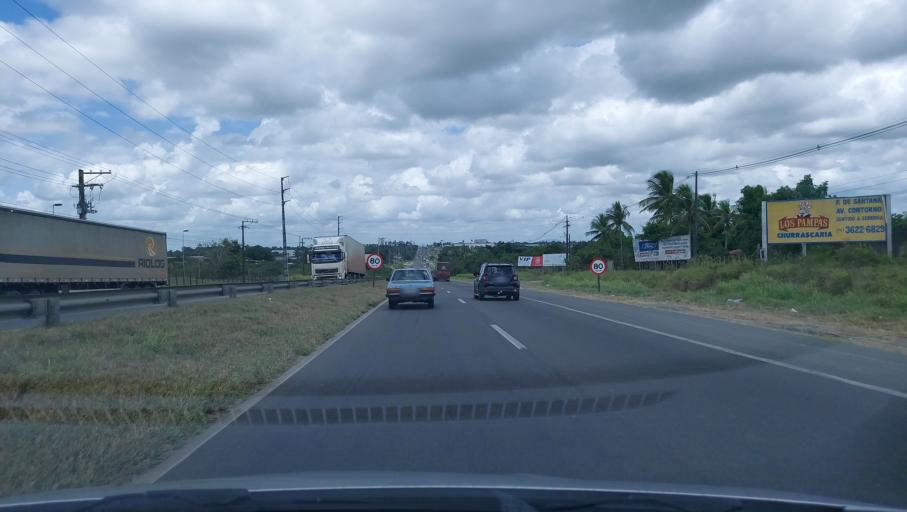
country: BR
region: Bahia
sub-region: Conceicao Do Jacuipe
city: Conceicao do Jacuipe
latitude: -12.3292
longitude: -38.8598
